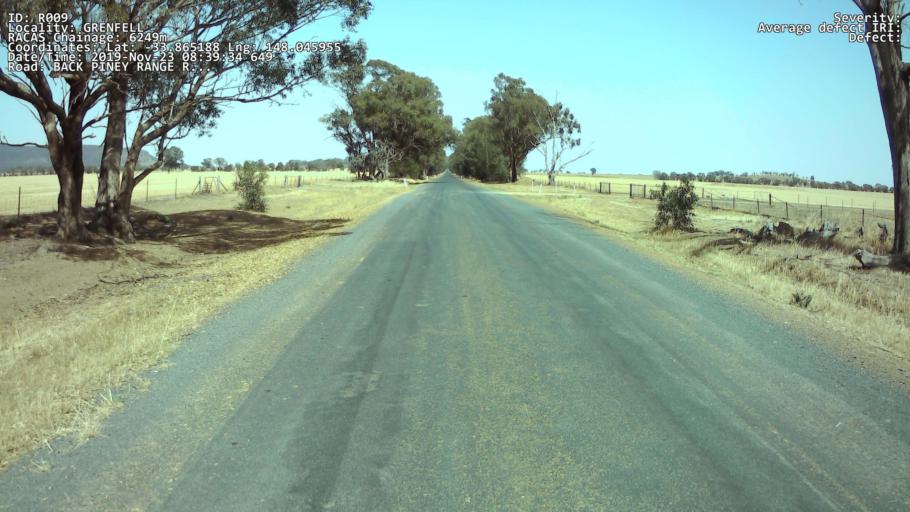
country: AU
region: New South Wales
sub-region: Weddin
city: Grenfell
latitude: -33.8652
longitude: 148.0459
